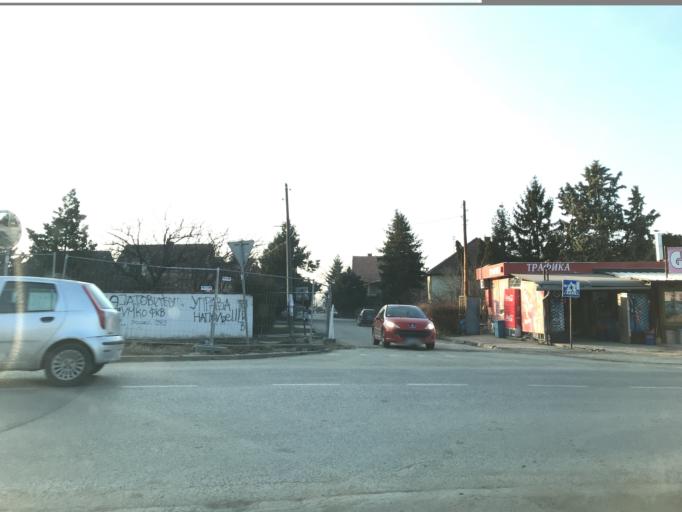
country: RS
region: Autonomna Pokrajina Vojvodina
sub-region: Juznobacki Okrug
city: Petrovaradin
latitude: 45.2229
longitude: 19.8552
